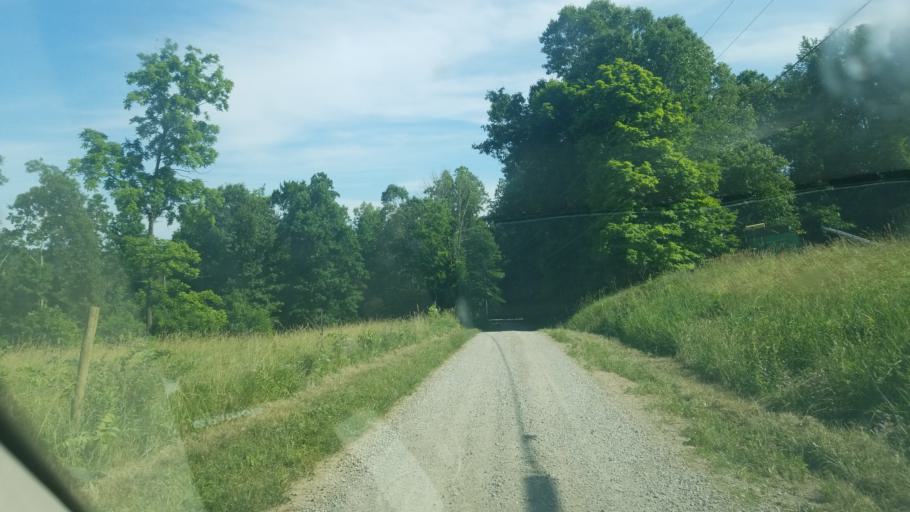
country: US
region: Ohio
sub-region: Holmes County
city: Millersburg
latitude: 40.4718
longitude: -81.9642
